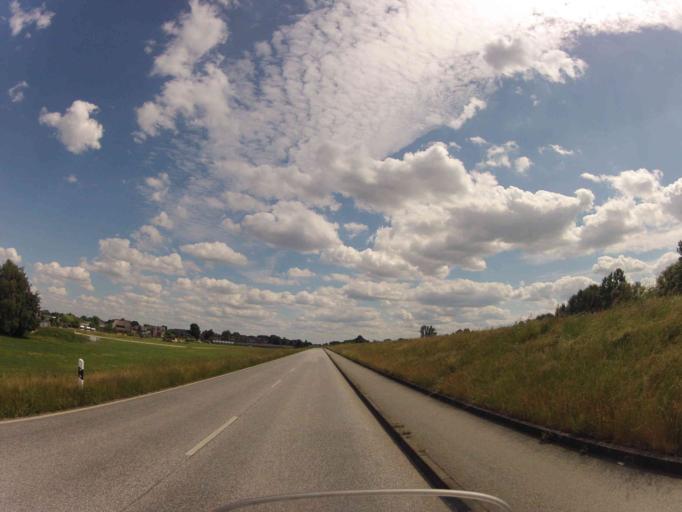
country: DE
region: Lower Saxony
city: Stelle
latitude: 53.4093
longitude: 10.1549
